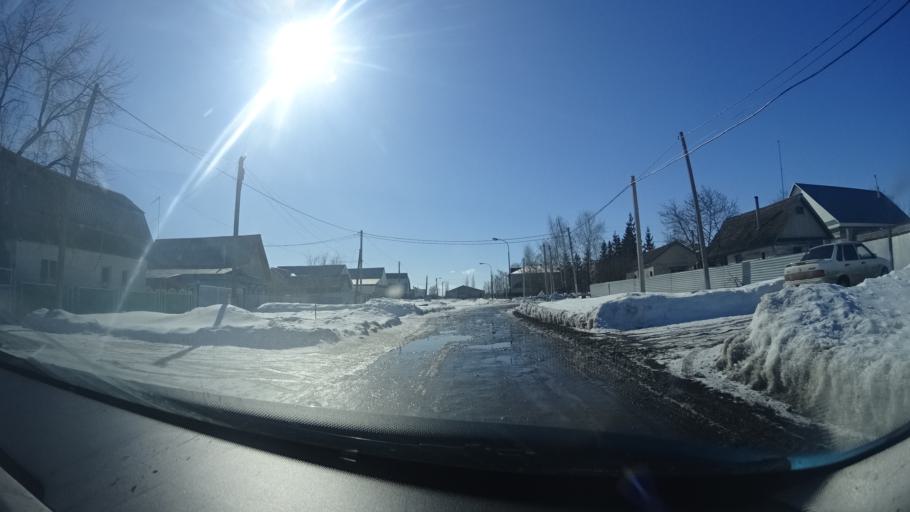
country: RU
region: Bashkortostan
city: Chishmy
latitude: 54.5779
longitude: 55.3763
